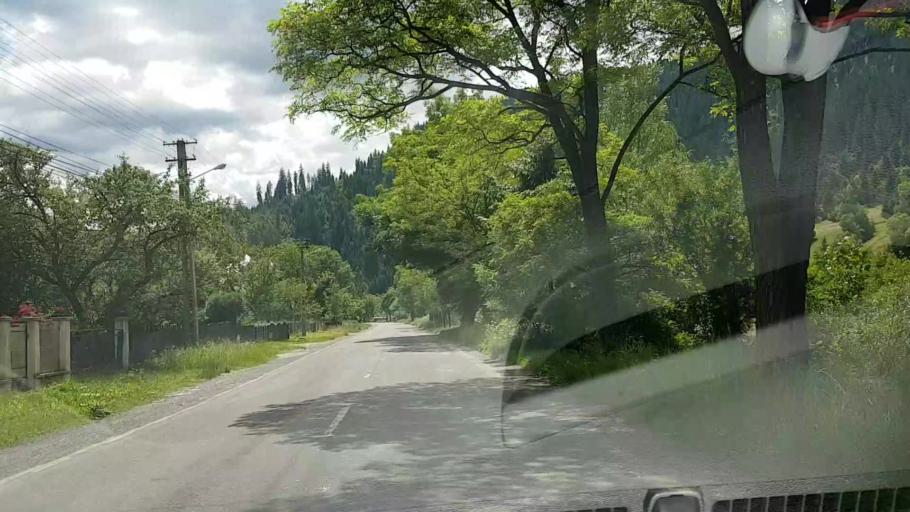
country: RO
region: Suceava
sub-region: Comuna Brosteni
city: Brosteni
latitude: 47.2443
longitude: 25.6912
